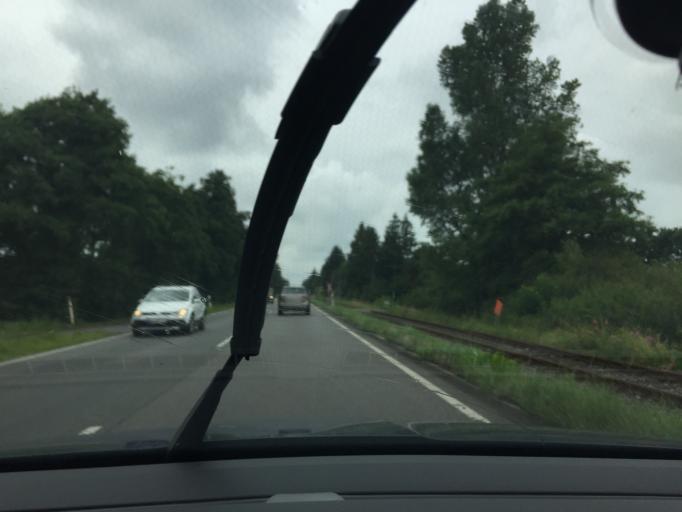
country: DE
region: Lower Saxony
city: Aurich
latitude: 53.4725
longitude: 7.4439
